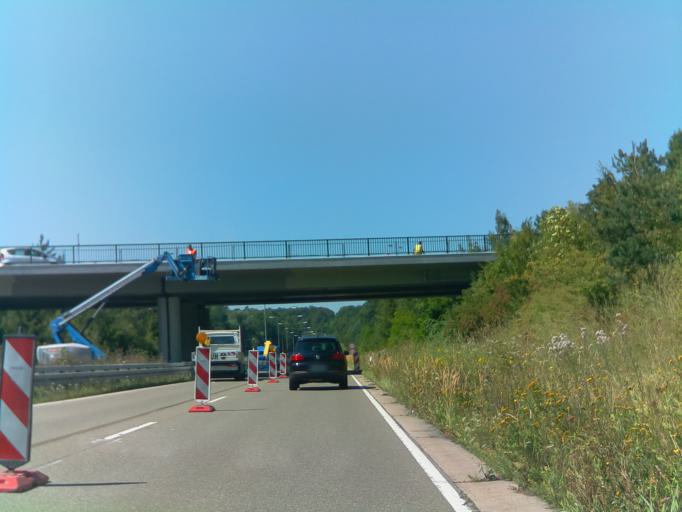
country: DE
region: Baden-Wuerttemberg
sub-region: Regierungsbezirk Stuttgart
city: Gerlingen
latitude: 48.7780
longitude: 9.0910
